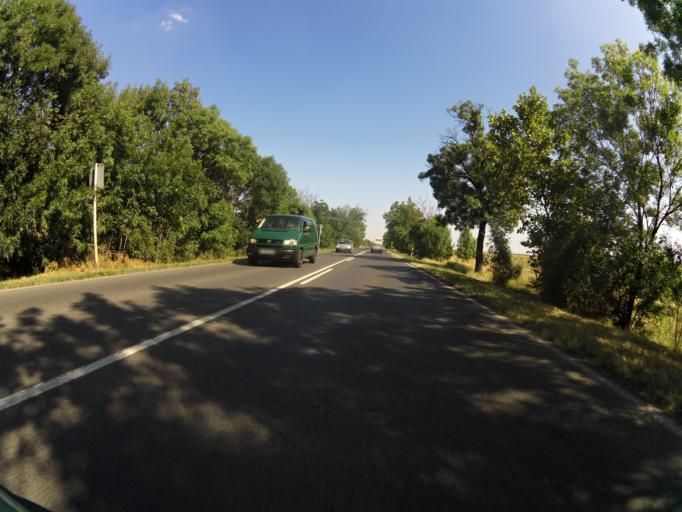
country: HU
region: Csongrad
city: Szatymaz
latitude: 46.3002
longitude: 20.0740
